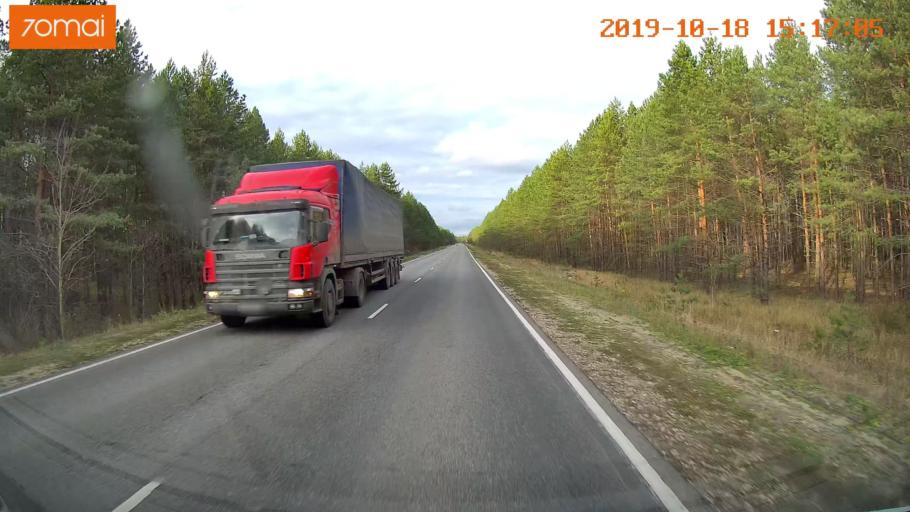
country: RU
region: Vladimir
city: Anopino
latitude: 55.6444
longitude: 40.7258
